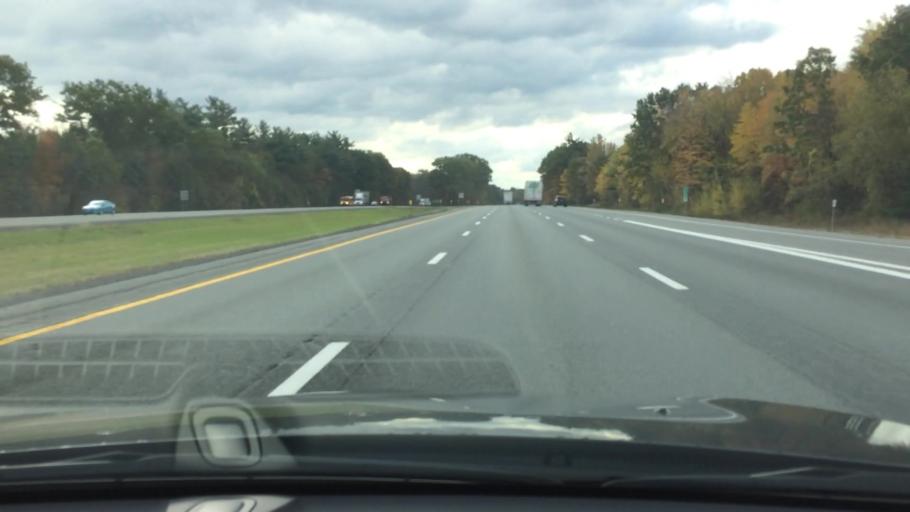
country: US
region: New York
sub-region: Saratoga County
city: Country Knolls
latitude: 42.9680
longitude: -73.8019
